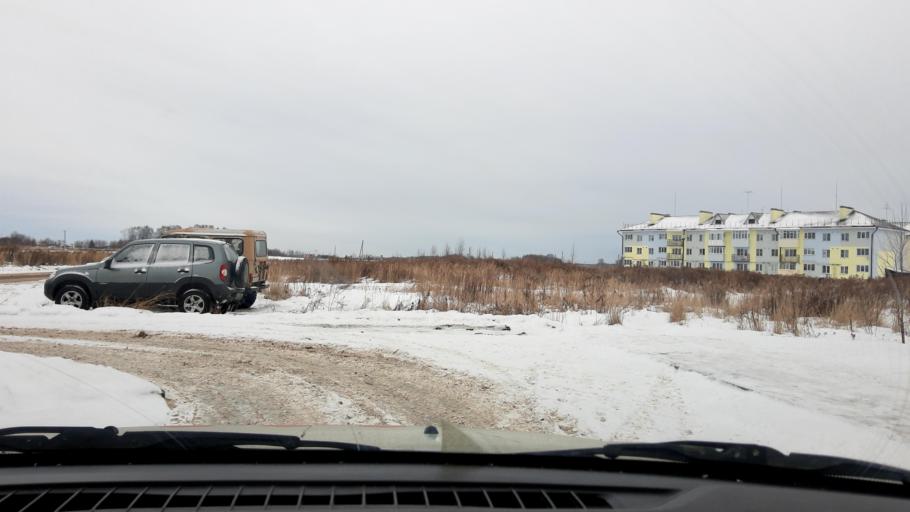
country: RU
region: Nizjnij Novgorod
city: Gorodets
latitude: 56.6689
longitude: 43.4769
